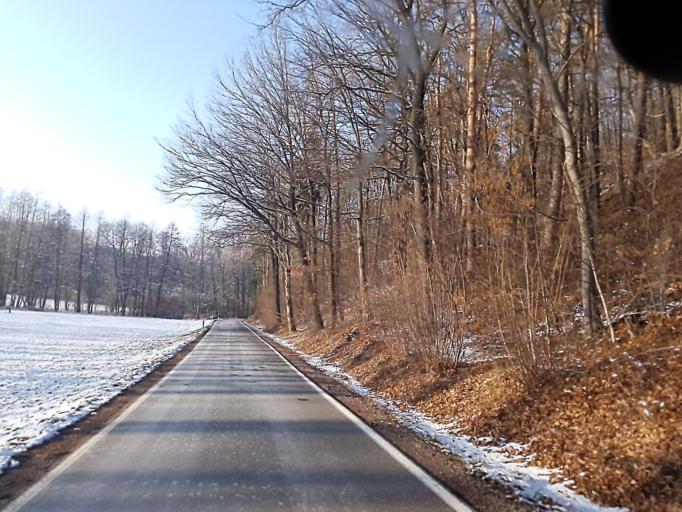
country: DE
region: Saxony
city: Hartha
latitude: 51.1480
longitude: 12.9777
